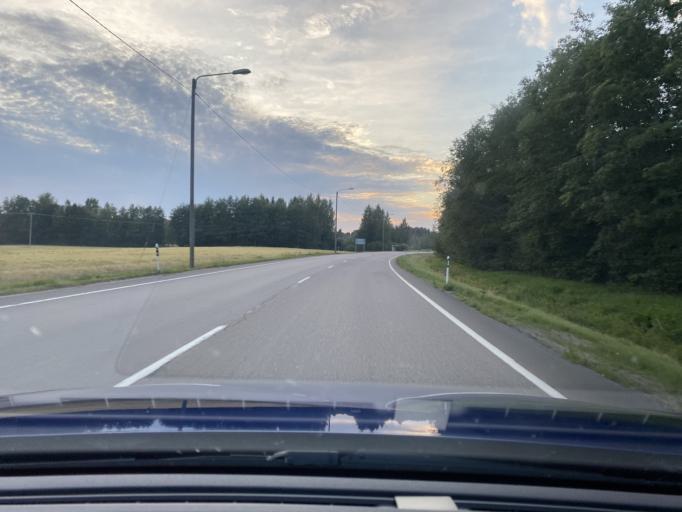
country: FI
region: Satakunta
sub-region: Pohjois-Satakunta
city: Honkajoki
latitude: 61.8757
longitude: 22.2971
